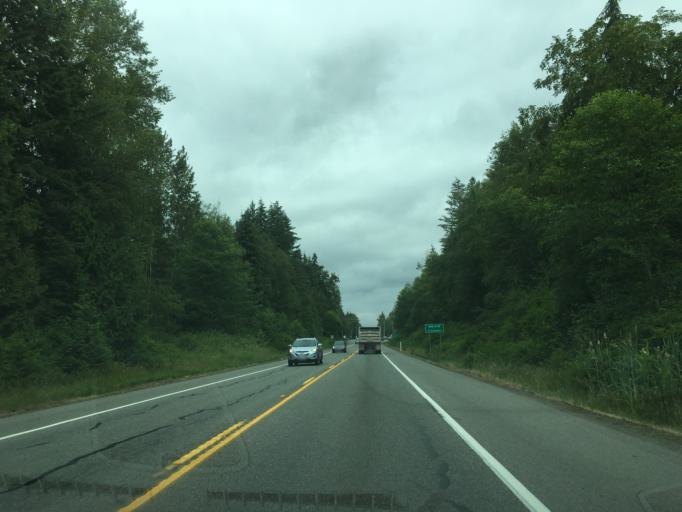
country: US
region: Washington
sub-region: Snohomish County
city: Sisco Heights
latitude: 48.0678
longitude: -122.1112
